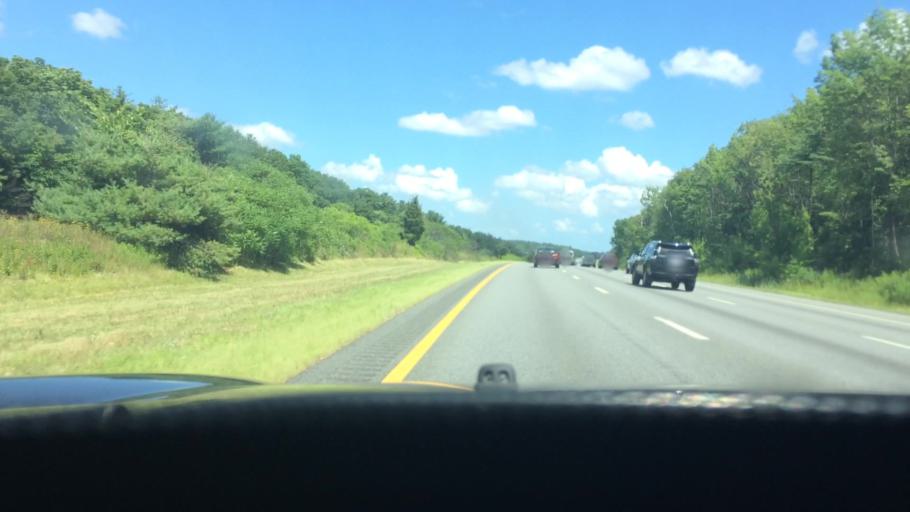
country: US
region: Massachusetts
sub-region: Middlesex County
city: Westford
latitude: 42.5760
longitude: -71.4153
